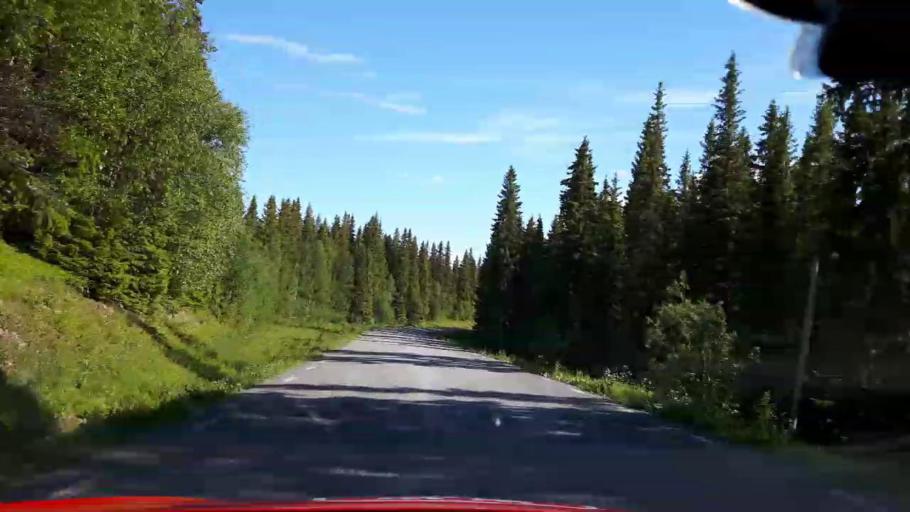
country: SE
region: Jaemtland
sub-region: Krokoms Kommun
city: Valla
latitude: 63.7277
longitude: 14.1208
